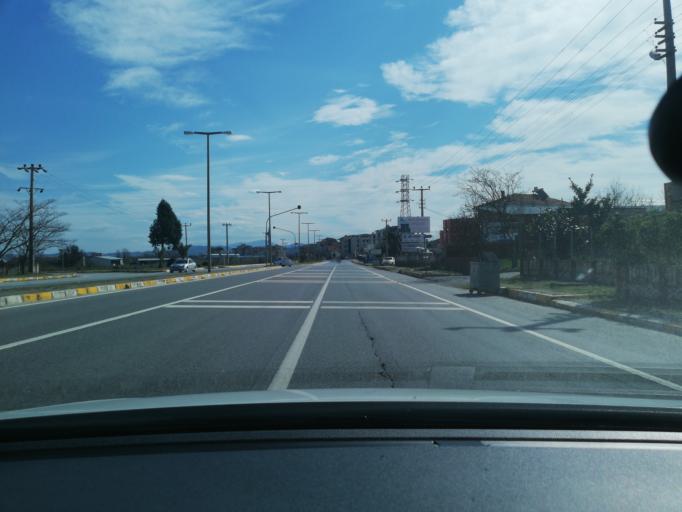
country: TR
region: Duzce
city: Akcakoca
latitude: 41.0849
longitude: 31.1684
